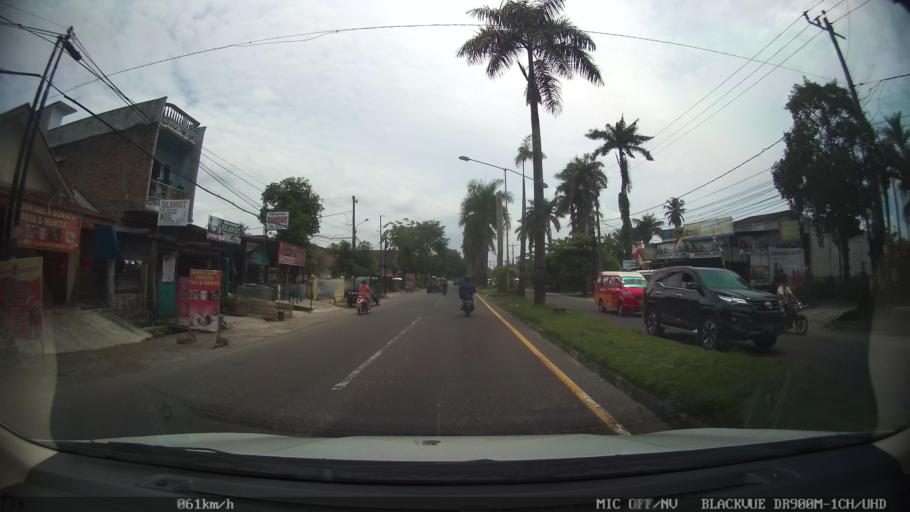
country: ID
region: North Sumatra
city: Sunggal
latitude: 3.5229
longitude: 98.6256
